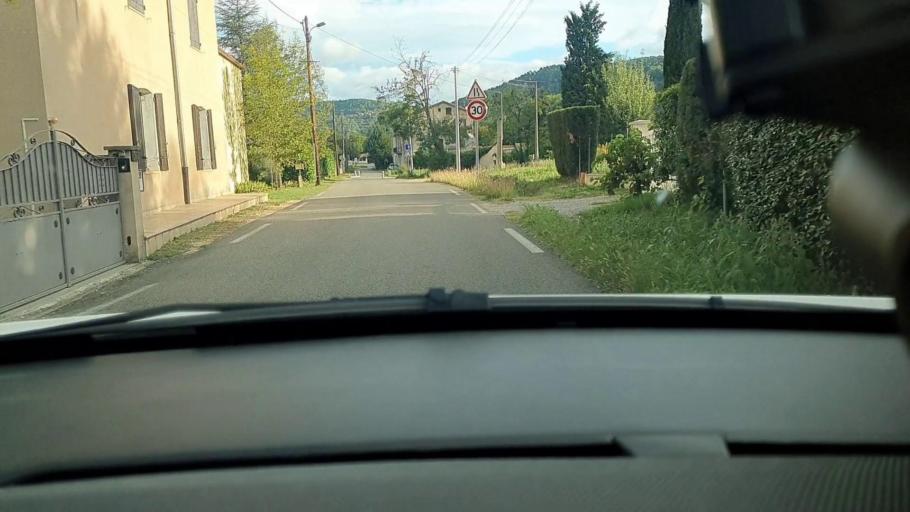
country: FR
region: Languedoc-Roussillon
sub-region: Departement du Gard
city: Besseges
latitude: 44.3129
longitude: 4.1303
